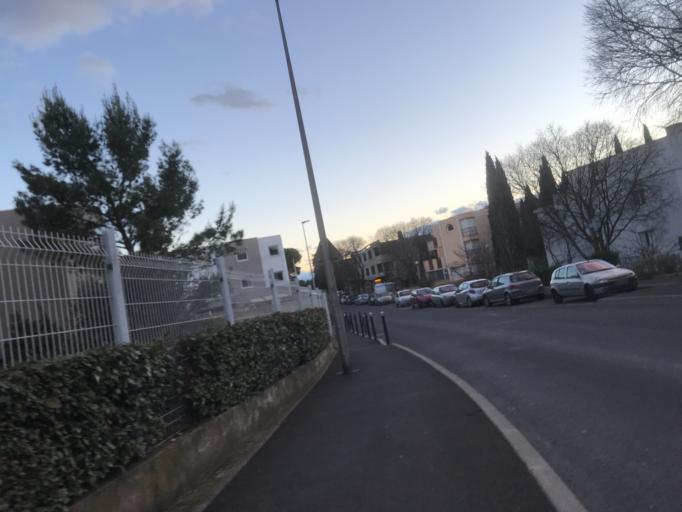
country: FR
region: Languedoc-Roussillon
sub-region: Departement de l'Herault
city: Montpellier
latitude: 43.6377
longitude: 3.8693
